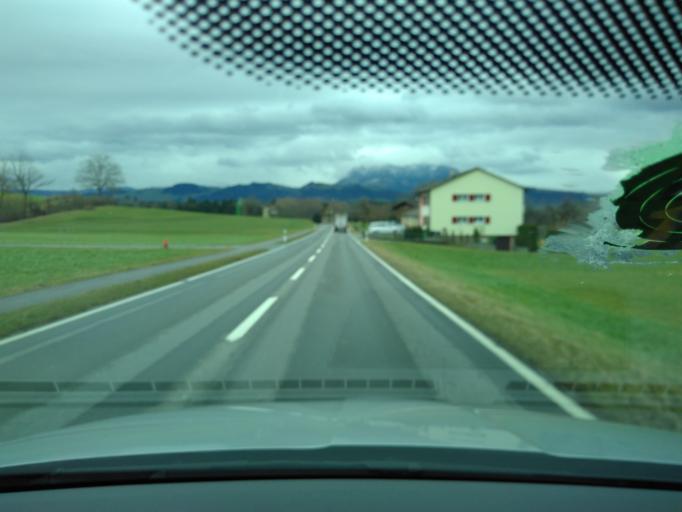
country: CH
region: Lucerne
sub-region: Hochdorf District
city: Ballwil
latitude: 47.1280
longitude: 8.3006
